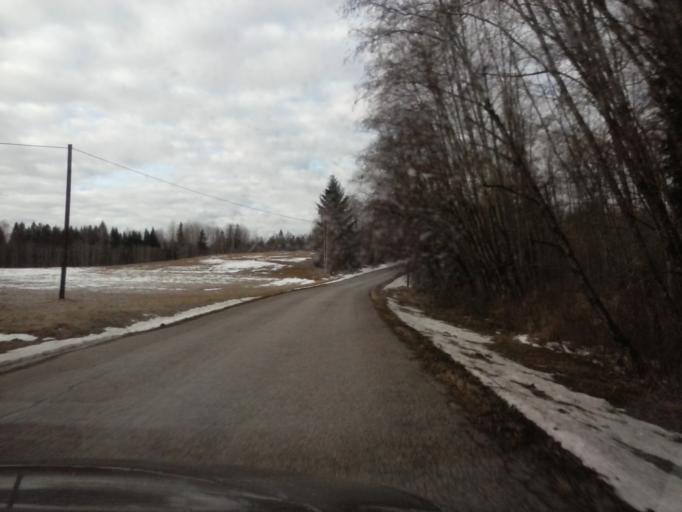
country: EE
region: Tartu
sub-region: Elva linn
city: Elva
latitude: 58.0046
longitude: 26.2883
